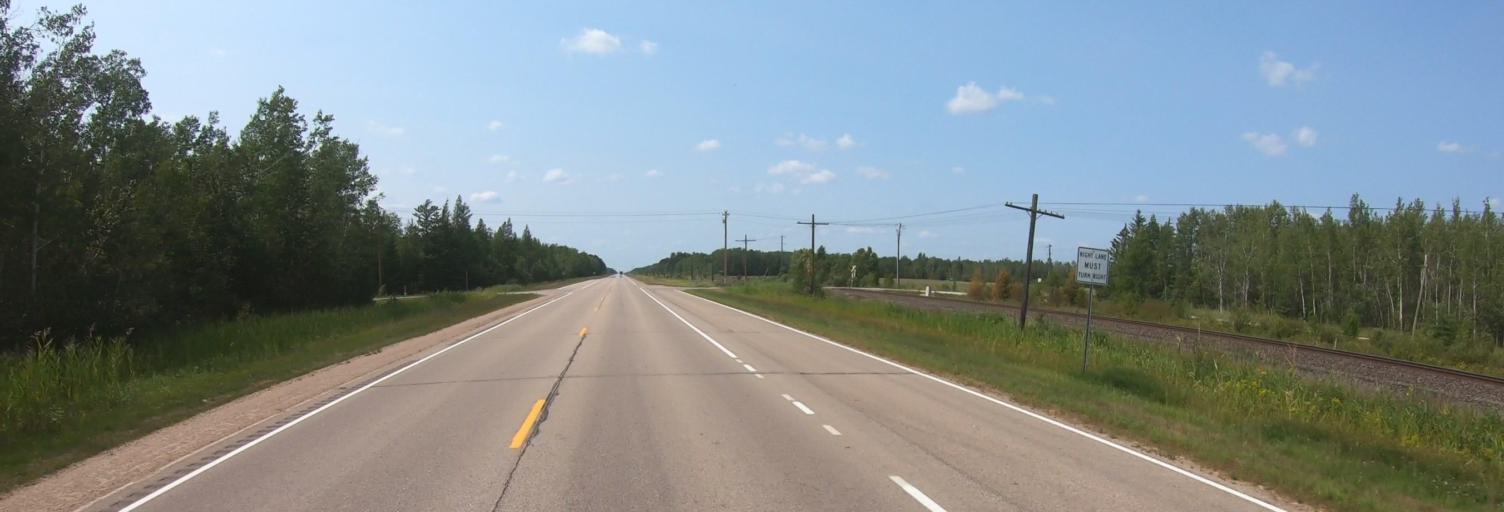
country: US
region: Minnesota
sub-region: Roseau County
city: Warroad
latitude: 48.7732
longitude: -94.9798
